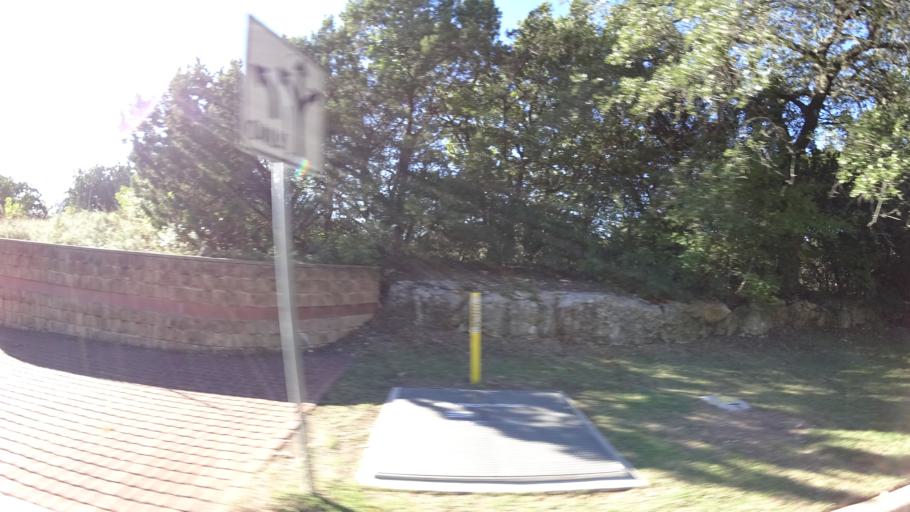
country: US
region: Texas
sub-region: Travis County
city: West Lake Hills
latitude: 30.3528
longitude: -97.7964
